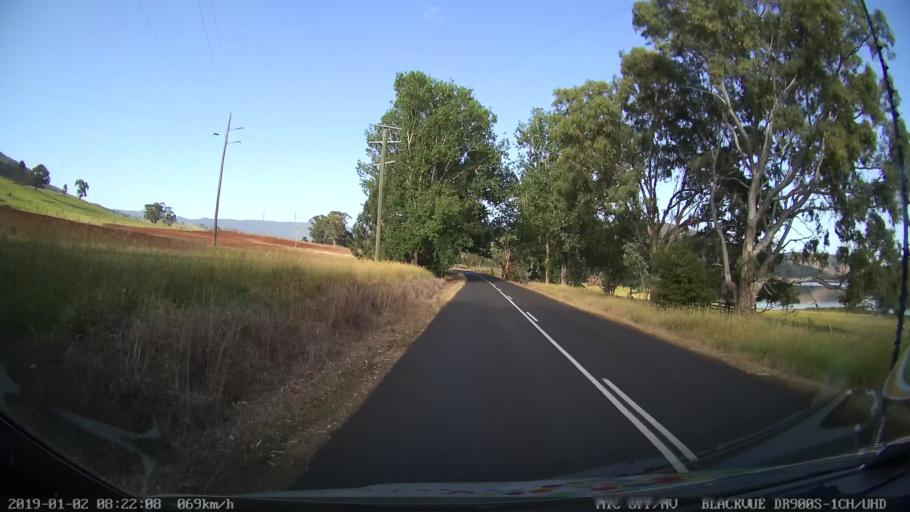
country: AU
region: New South Wales
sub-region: Tumut Shire
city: Tumut
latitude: -35.5696
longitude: 148.3188
